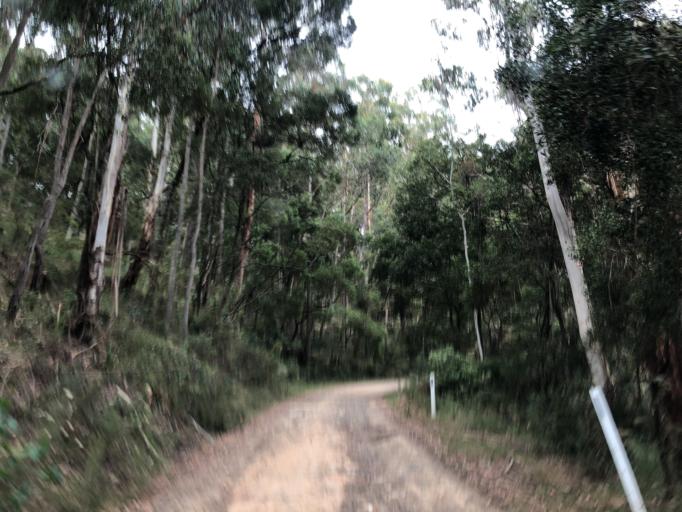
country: AU
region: Victoria
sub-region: Moorabool
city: Bacchus Marsh
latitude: -37.4721
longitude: 144.3253
